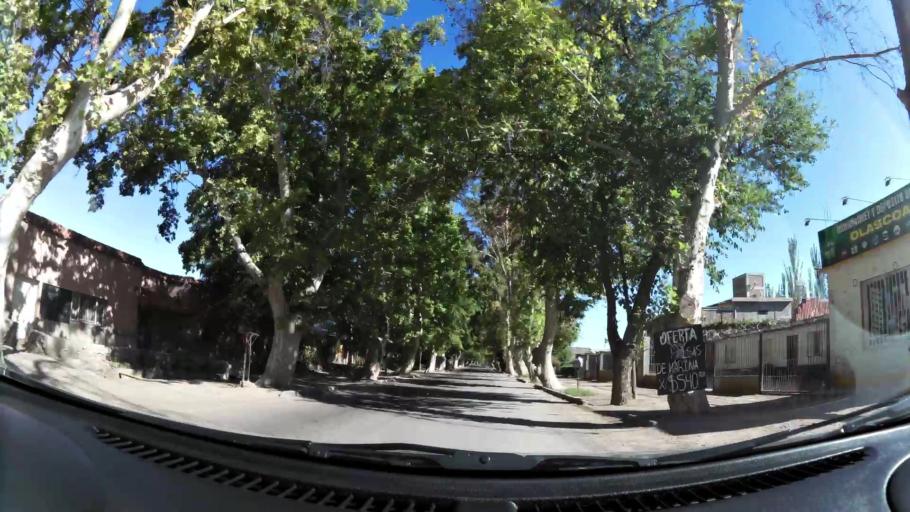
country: AR
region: Mendoza
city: Las Heras
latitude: -32.8330
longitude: -68.8246
